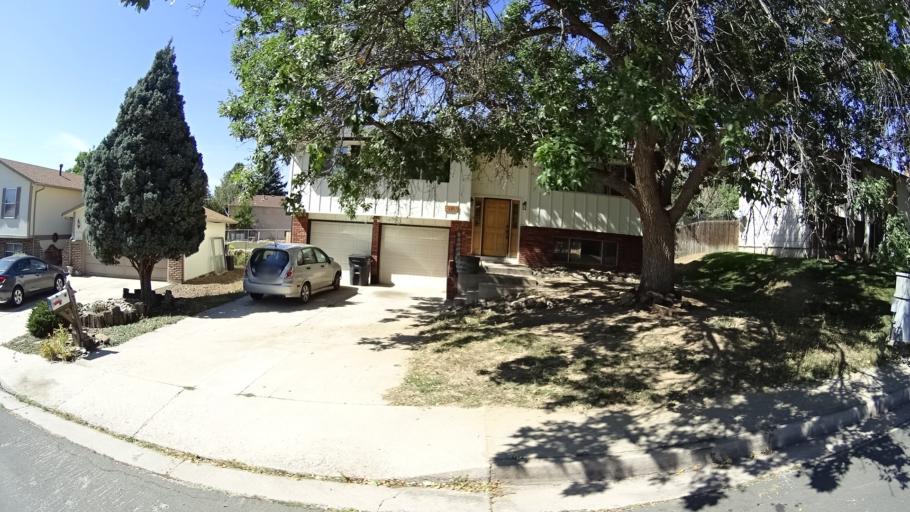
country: US
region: Colorado
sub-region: El Paso County
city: Cimarron Hills
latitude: 38.9078
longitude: -104.7655
